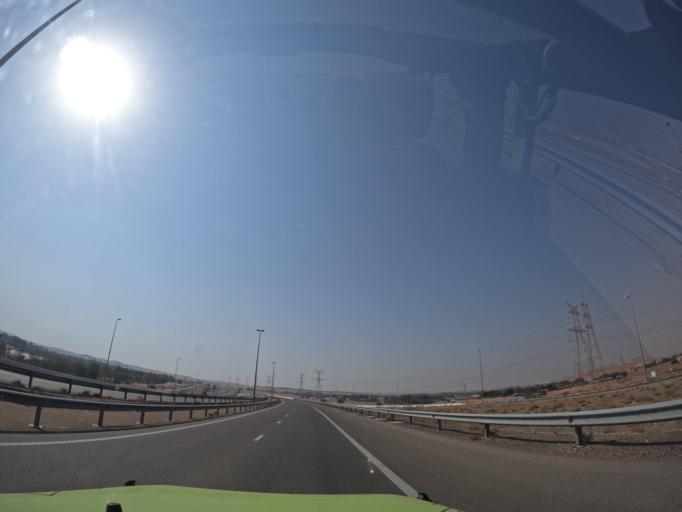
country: OM
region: Al Buraimi
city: Al Buraymi
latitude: 24.3688
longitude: 55.7283
